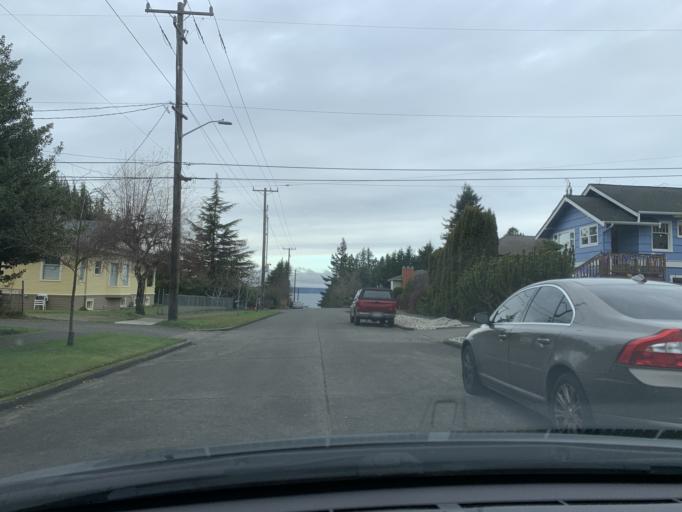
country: US
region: Washington
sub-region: King County
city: White Center
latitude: 47.5522
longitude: -122.3902
